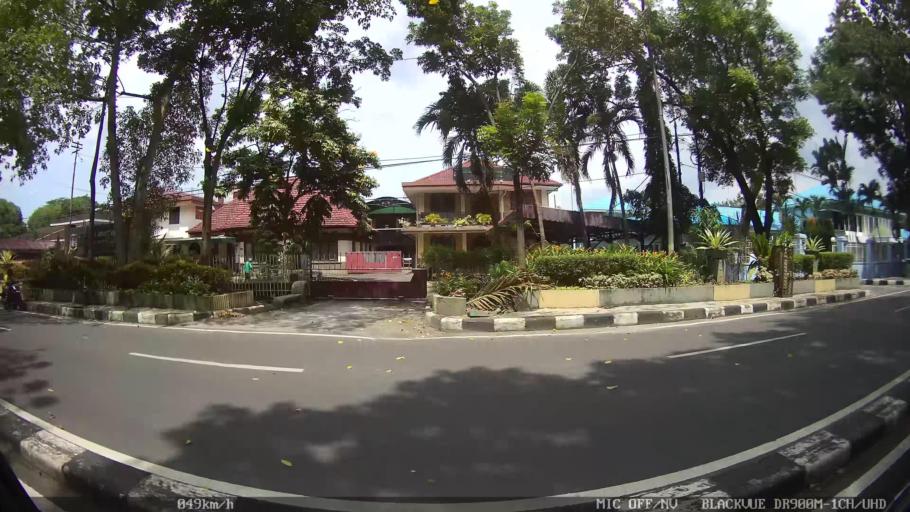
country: ID
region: North Sumatra
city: Medan
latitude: 3.5732
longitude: 98.6778
